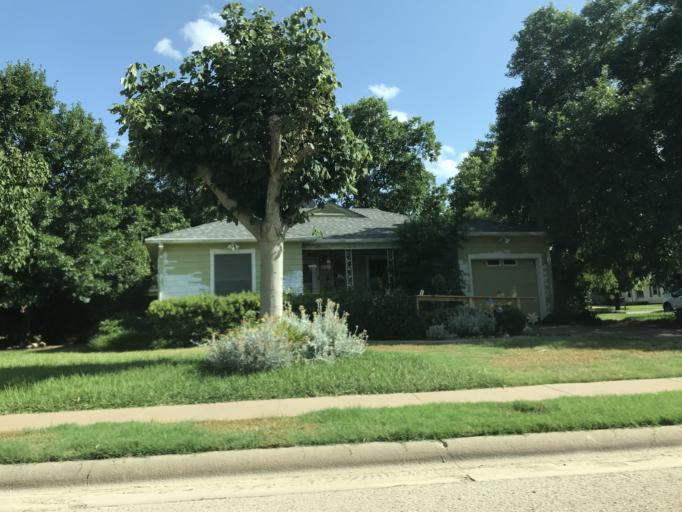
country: US
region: Texas
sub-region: Taylor County
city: Abilene
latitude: 32.4298
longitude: -99.7621
